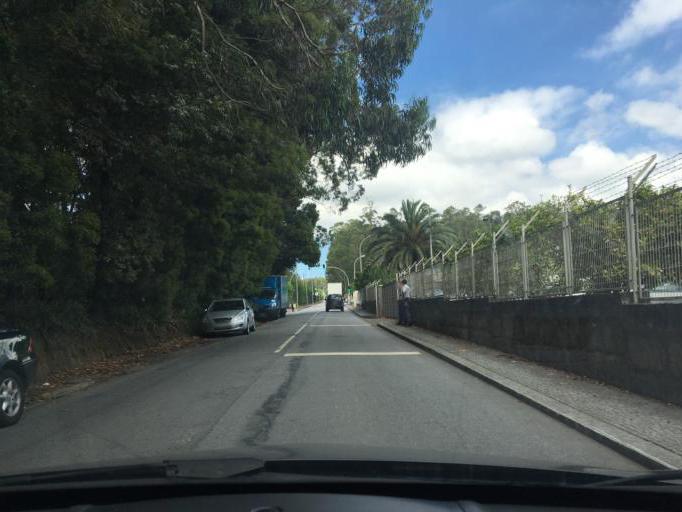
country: PT
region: Porto
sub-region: Maia
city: Anta
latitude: 41.2902
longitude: -8.6087
